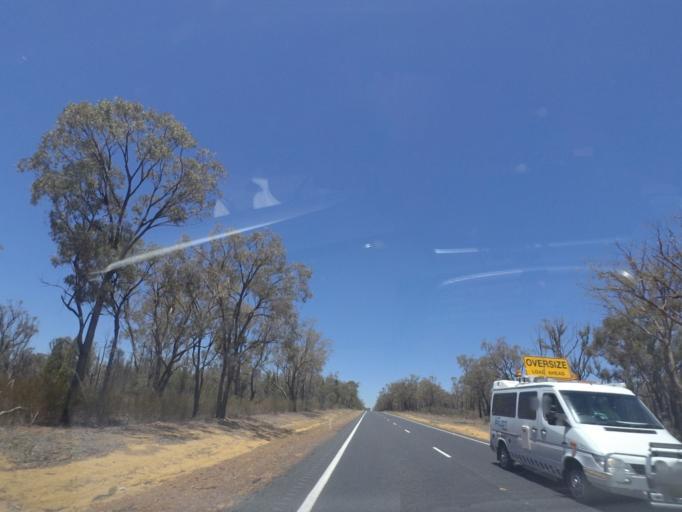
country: AU
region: New South Wales
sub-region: Narrabri
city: Narrabri
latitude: -30.7413
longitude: 149.5153
